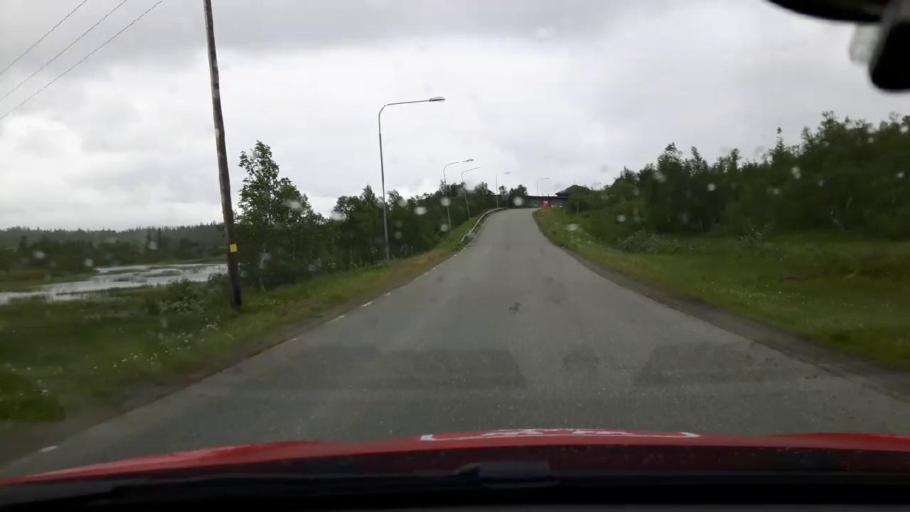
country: NO
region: Nord-Trondelag
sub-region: Meraker
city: Meraker
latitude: 63.3116
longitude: 12.1113
